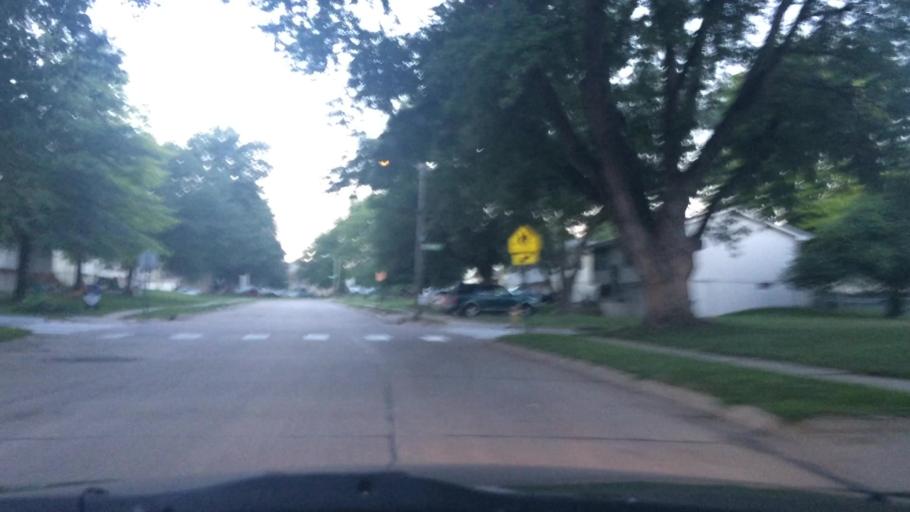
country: US
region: Nebraska
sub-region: Sarpy County
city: La Vista
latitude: 41.1848
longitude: -96.0503
